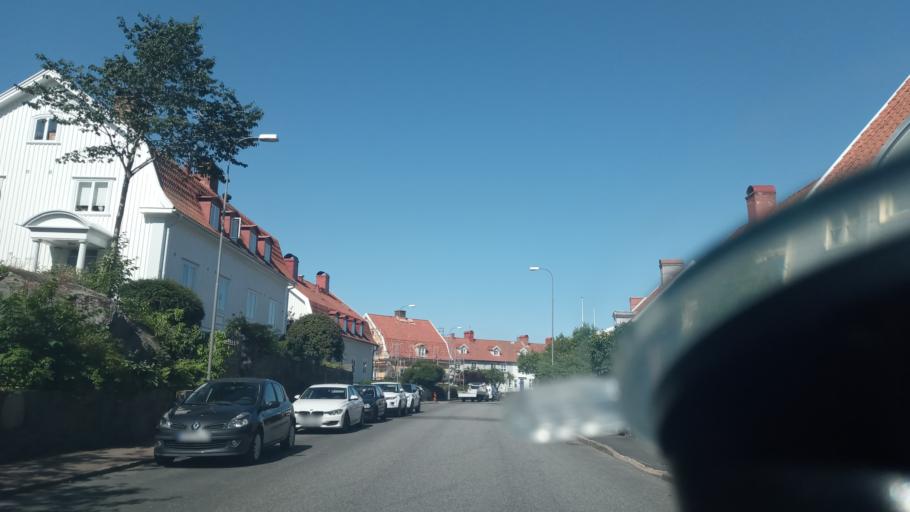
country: SE
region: Vaestra Goetaland
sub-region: Molndal
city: Moelndal
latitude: 57.6959
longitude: 12.0082
